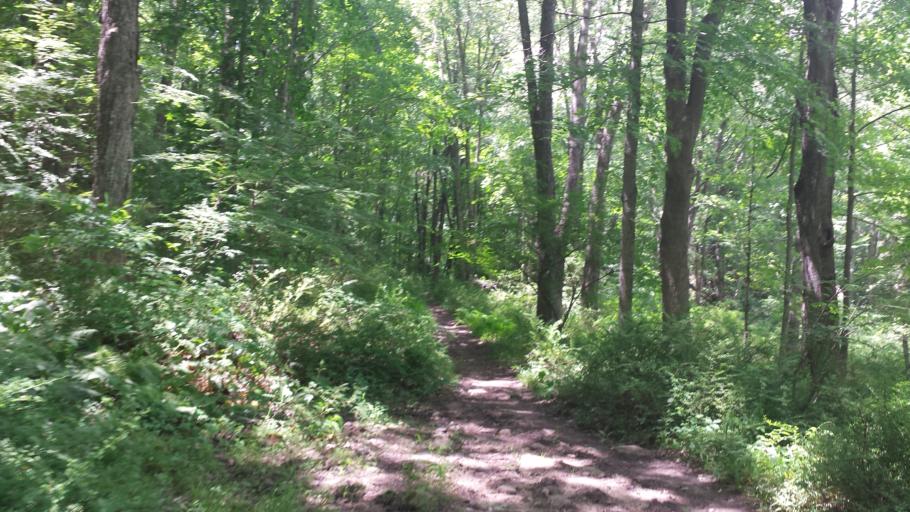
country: US
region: New York
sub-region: Westchester County
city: Pound Ridge
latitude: 41.2697
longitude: -73.5764
